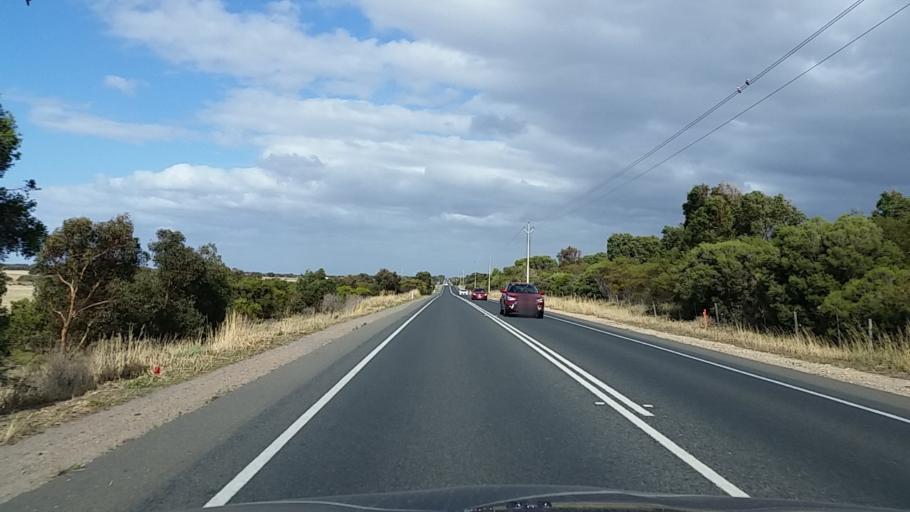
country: AU
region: South Australia
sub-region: Alexandrina
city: Goolwa
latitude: -35.5075
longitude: 138.7457
